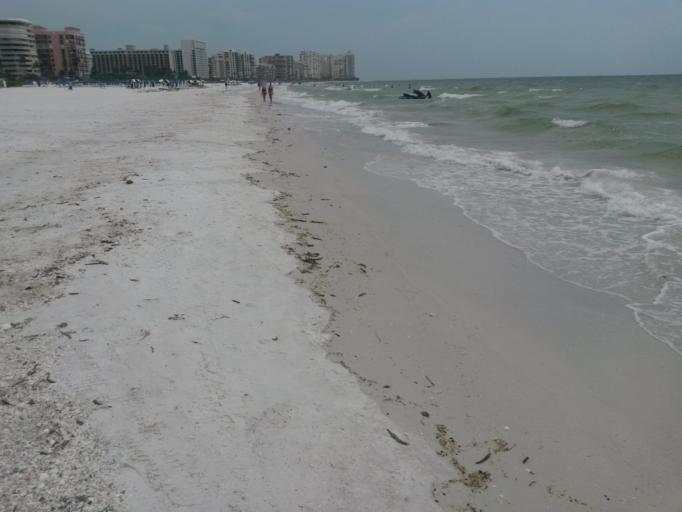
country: US
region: Florida
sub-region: Collier County
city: Marco
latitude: 25.9269
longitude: -81.7309
